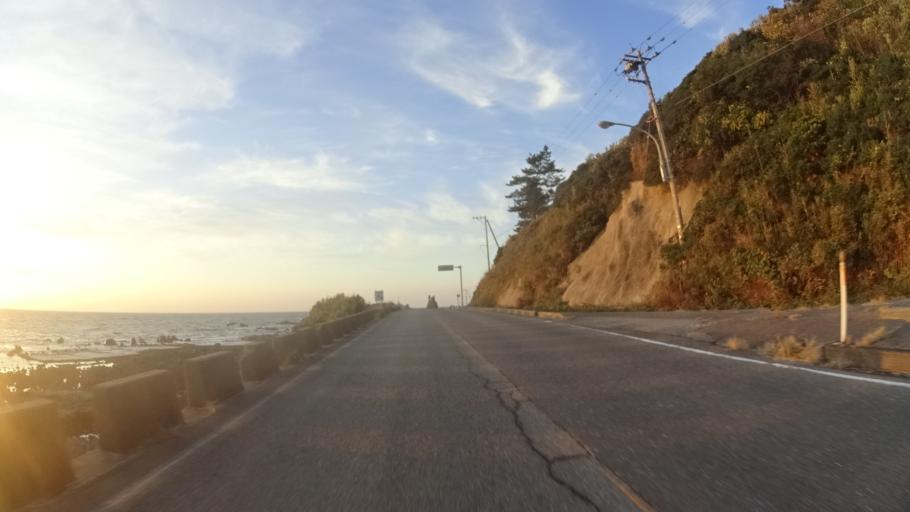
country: JP
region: Ishikawa
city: Nanao
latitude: 37.2344
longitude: 136.7030
